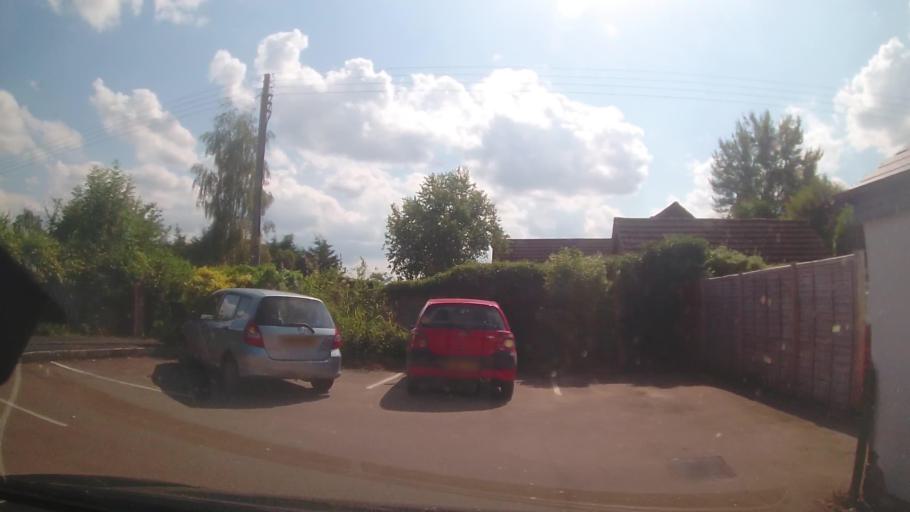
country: GB
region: England
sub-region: Herefordshire
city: Brockhampton
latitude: 52.0090
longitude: -2.6184
